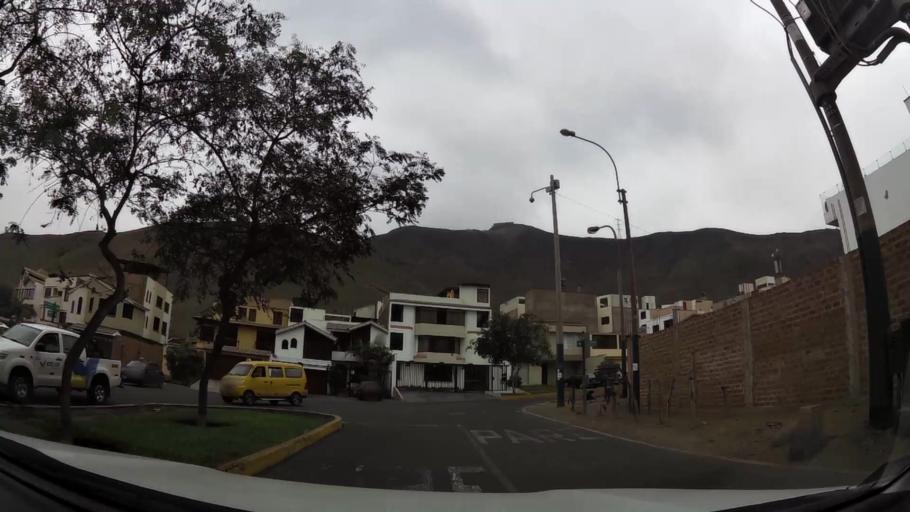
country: PE
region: Lima
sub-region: Lima
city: La Molina
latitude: -12.1038
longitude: -76.9567
